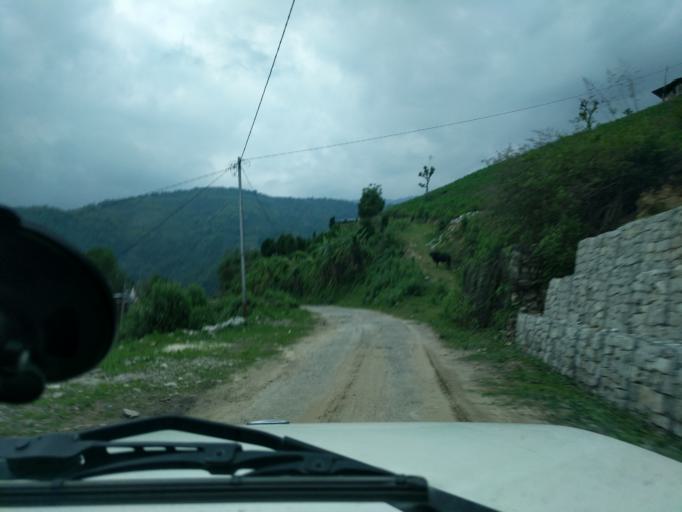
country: BT
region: Mongar
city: Mongar
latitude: 27.2996
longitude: 91.1498
